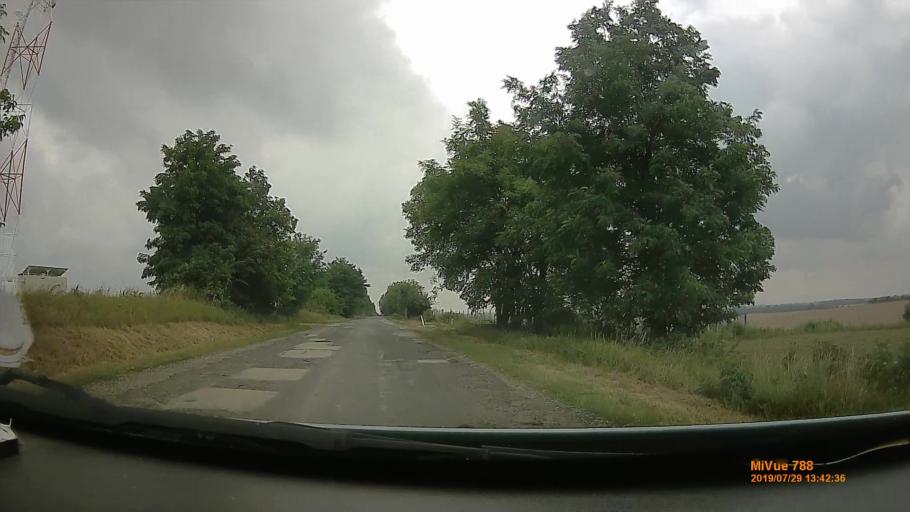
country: HU
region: Somogy
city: Balatonfoldvar
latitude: 46.8081
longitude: 17.9290
